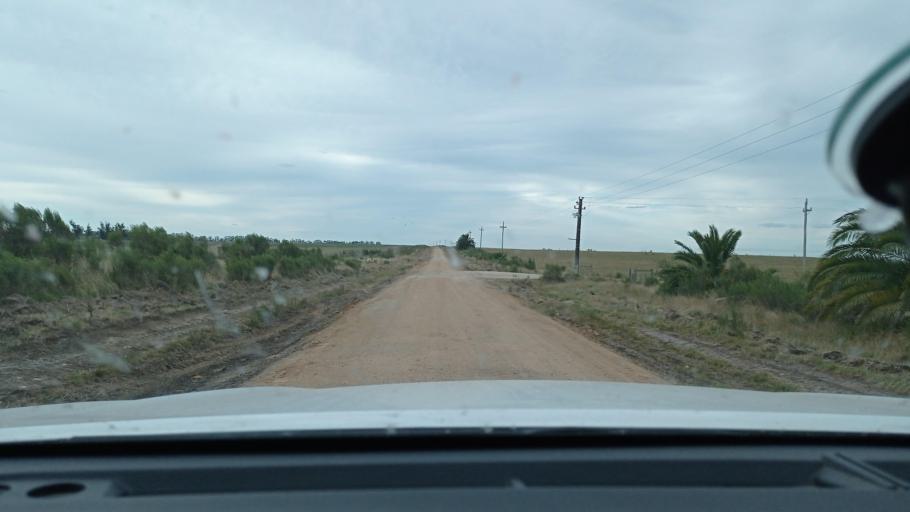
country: UY
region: Florida
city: Casupa
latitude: -34.1042
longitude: -55.7630
